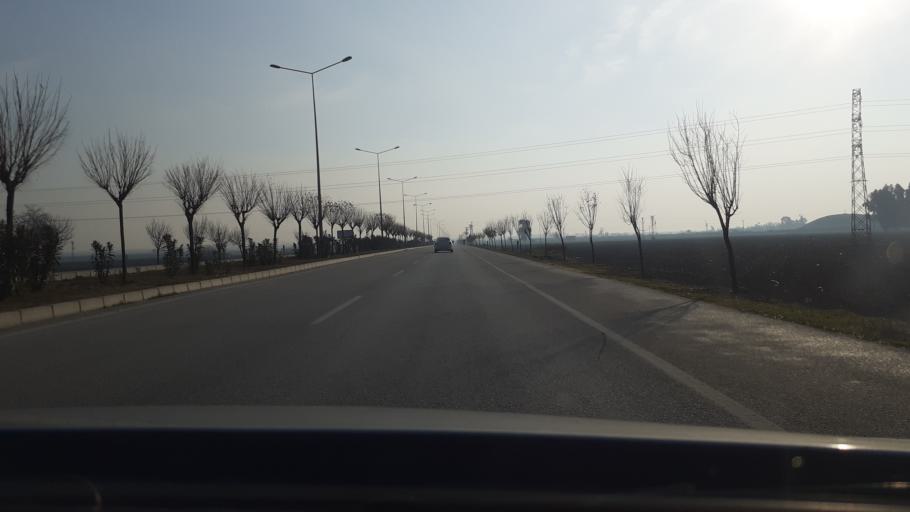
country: TR
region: Hatay
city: Serinyol
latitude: 36.3721
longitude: 36.2293
